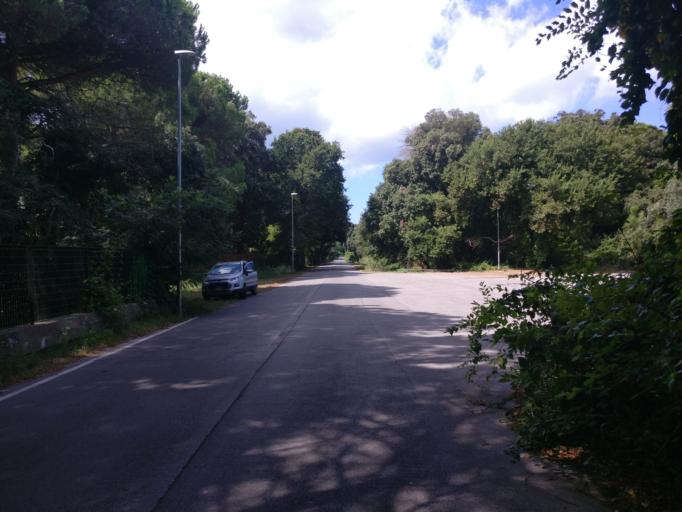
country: IT
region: Tuscany
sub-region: Province of Pisa
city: Marina di Pisa-Tirrenia-Calambrone
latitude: 43.6177
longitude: 10.3035
